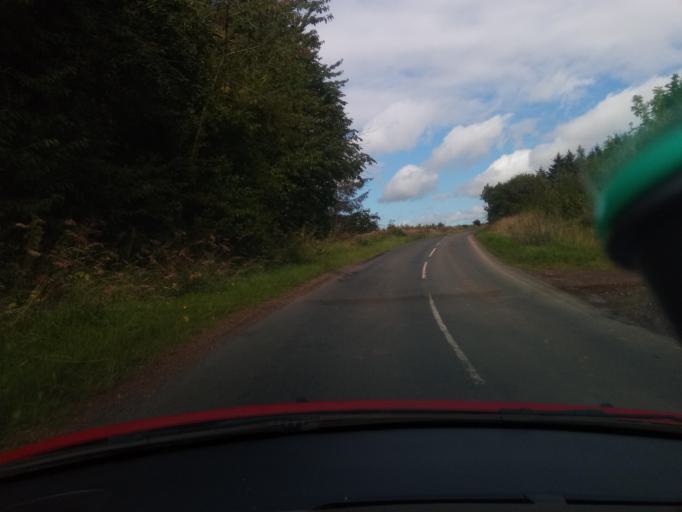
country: GB
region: Scotland
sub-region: The Scottish Borders
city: Melrose
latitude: 55.5706
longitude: -2.7312
